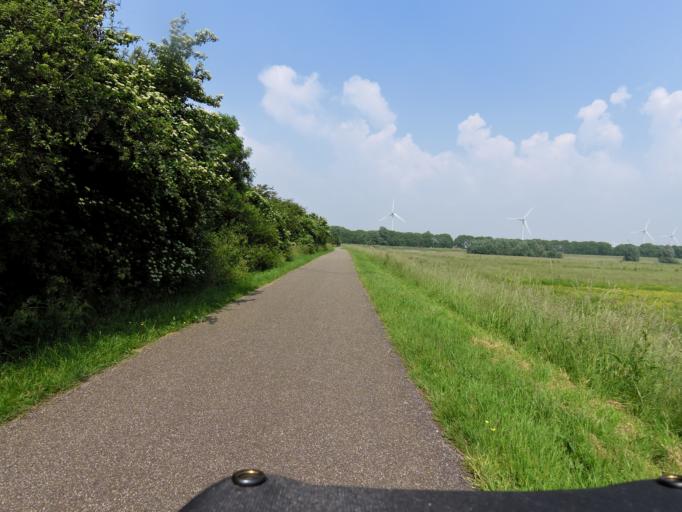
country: NL
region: South Holland
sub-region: Gemeente Maassluis
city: Maassluis
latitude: 51.8607
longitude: 4.2488
